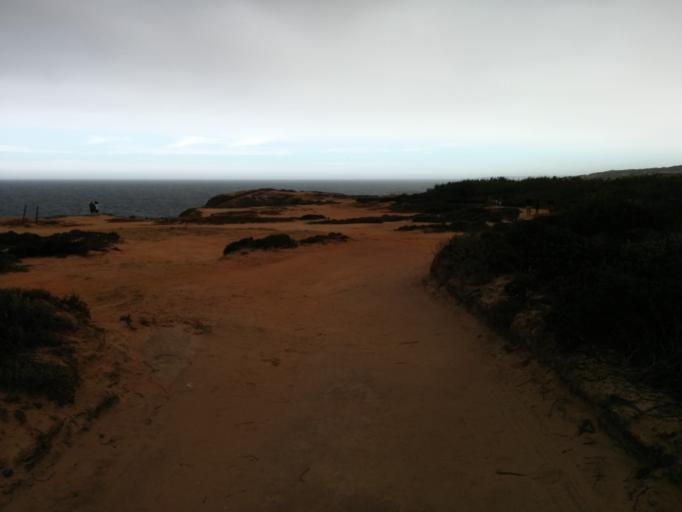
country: PT
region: Beja
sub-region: Odemira
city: Vila Nova de Milfontes
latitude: 37.5985
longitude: -8.8169
